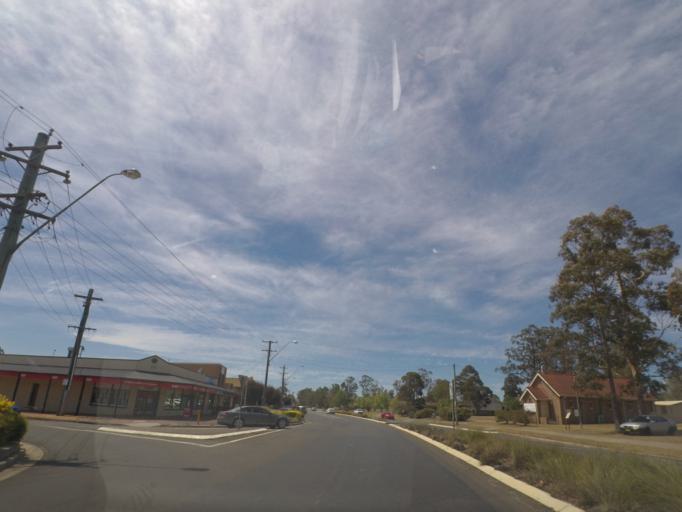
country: AU
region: New South Wales
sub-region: Wollondilly
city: Picton
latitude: -34.2247
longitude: 150.5927
